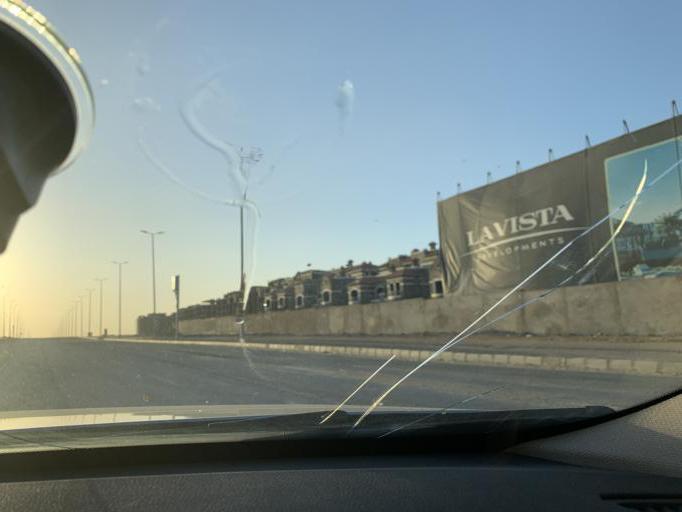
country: EG
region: Muhafazat al Qalyubiyah
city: Al Khankah
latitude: 30.0224
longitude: 31.5926
